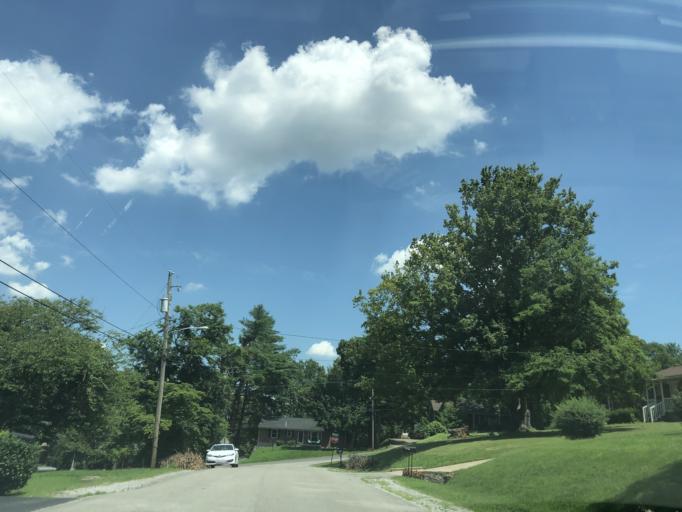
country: US
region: Tennessee
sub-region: Davidson County
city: Lakewood
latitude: 36.1770
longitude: -86.6496
